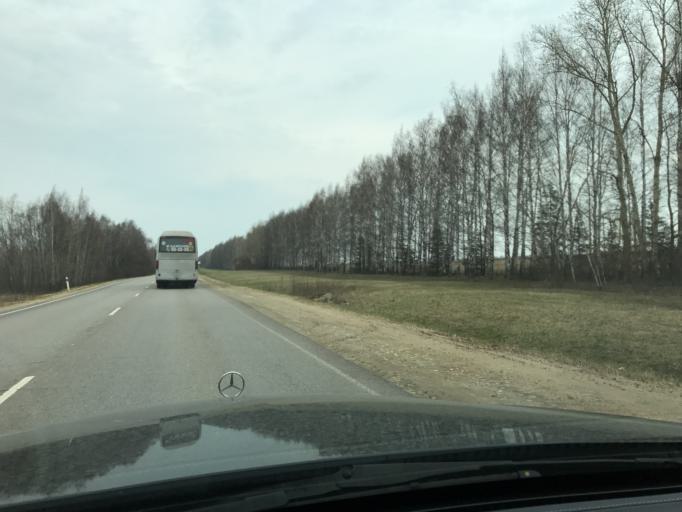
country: RU
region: Vladimir
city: Suzdal'
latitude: 56.3888
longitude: 40.4528
